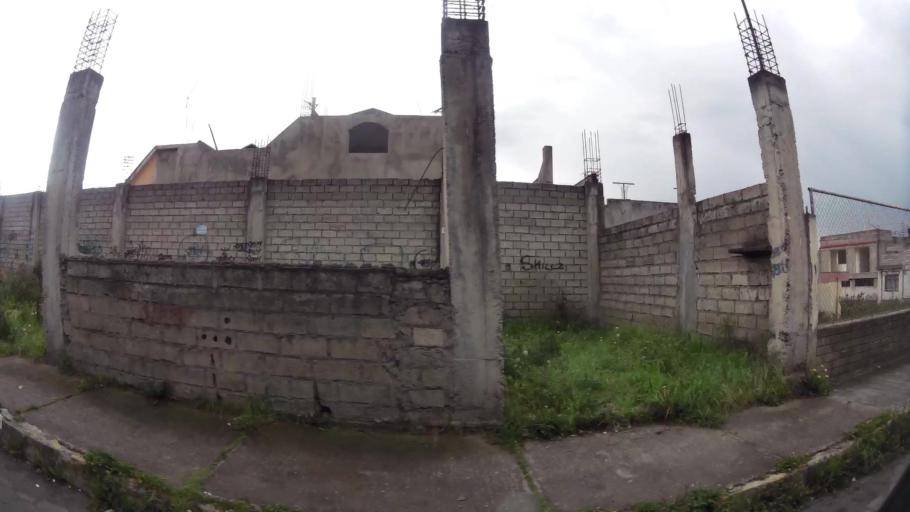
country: EC
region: Pichincha
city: Quito
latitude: -0.3096
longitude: -78.5531
